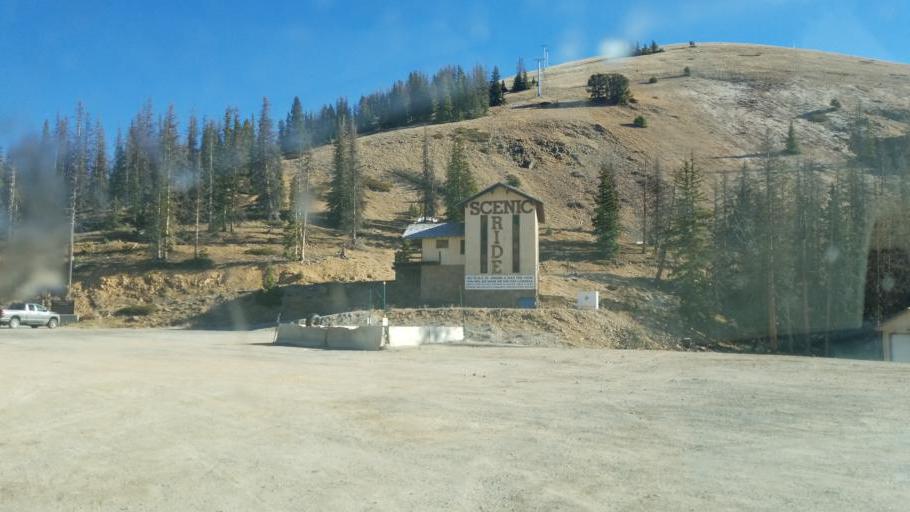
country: US
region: Colorado
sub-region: Chaffee County
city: Salida
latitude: 38.4956
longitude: -106.3255
